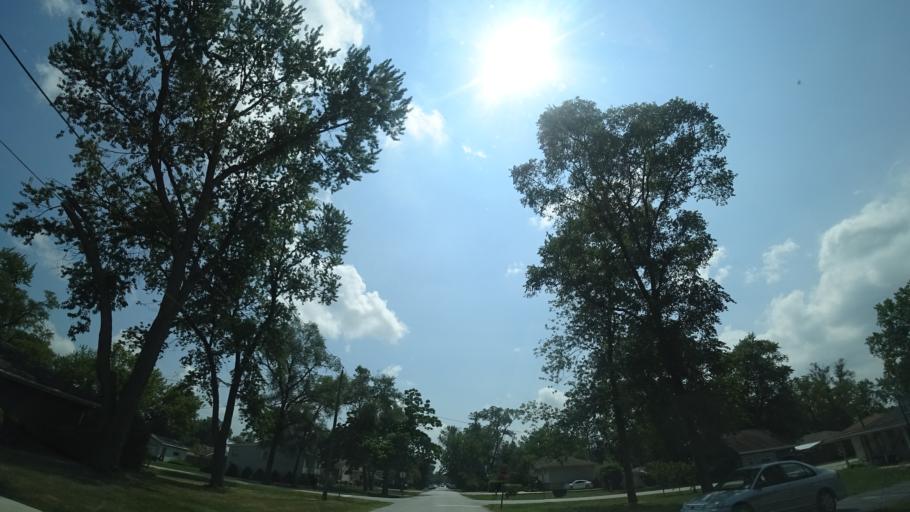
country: US
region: Illinois
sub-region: Cook County
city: Chicago Ridge
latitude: 41.6962
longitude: -87.7815
